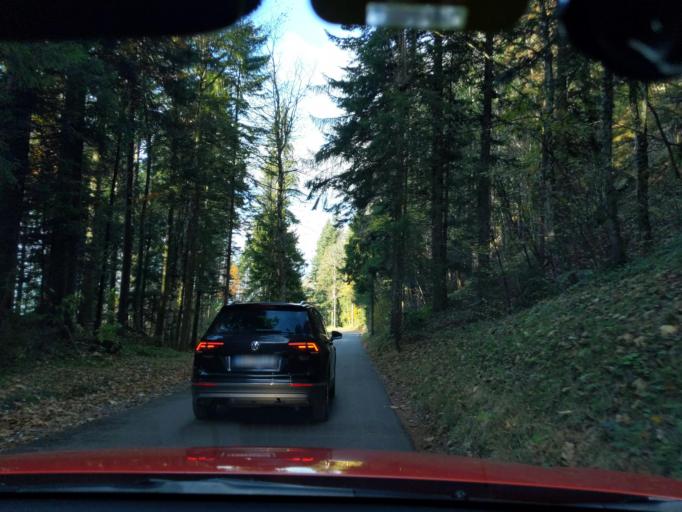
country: AT
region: Vorarlberg
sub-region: Politischer Bezirk Bregenz
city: Eichenberg
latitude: 47.5173
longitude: 9.7780
